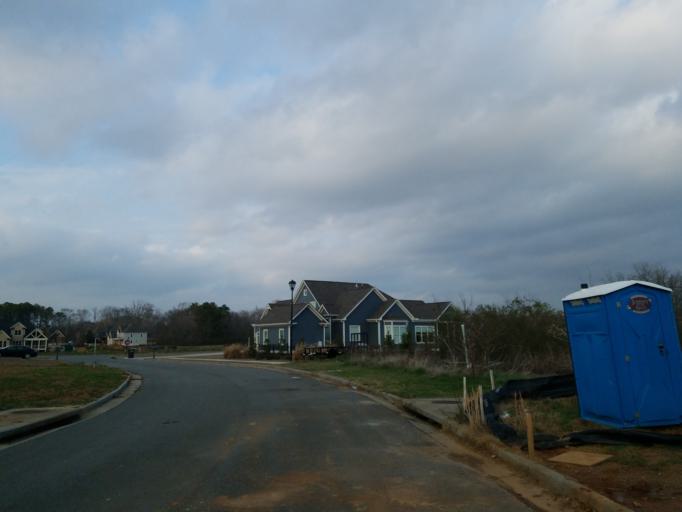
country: US
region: Georgia
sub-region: Bartow County
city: Cartersville
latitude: 34.1183
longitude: -84.8026
